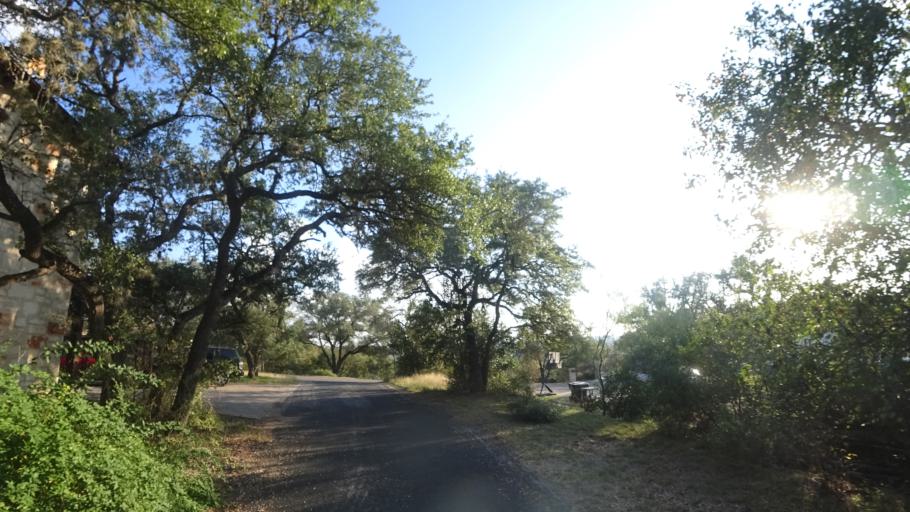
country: US
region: Texas
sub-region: Travis County
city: Lost Creek
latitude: 30.2959
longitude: -97.8472
